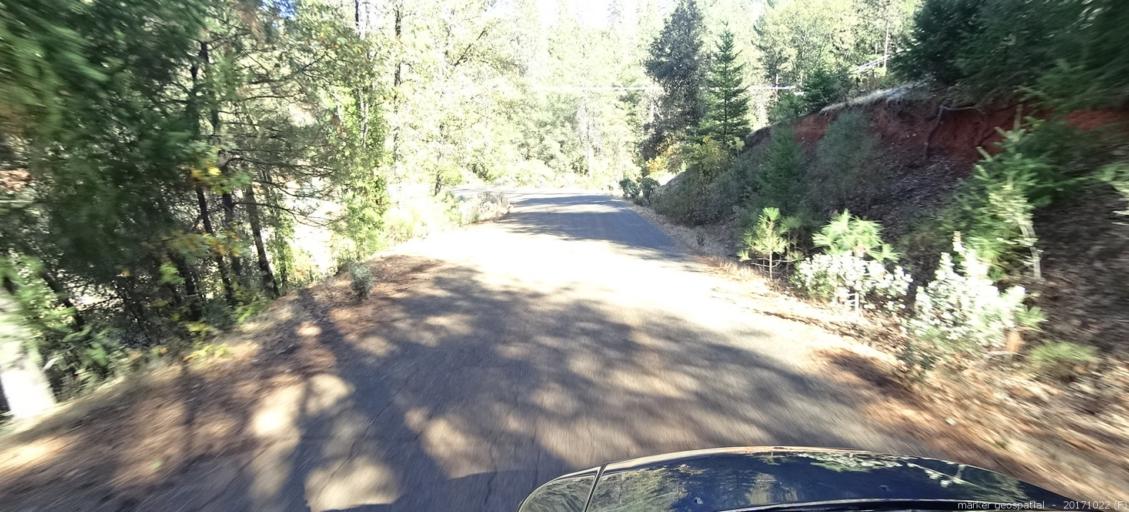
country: US
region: California
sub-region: Shasta County
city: Shasta Lake
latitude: 40.8853
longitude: -122.3686
